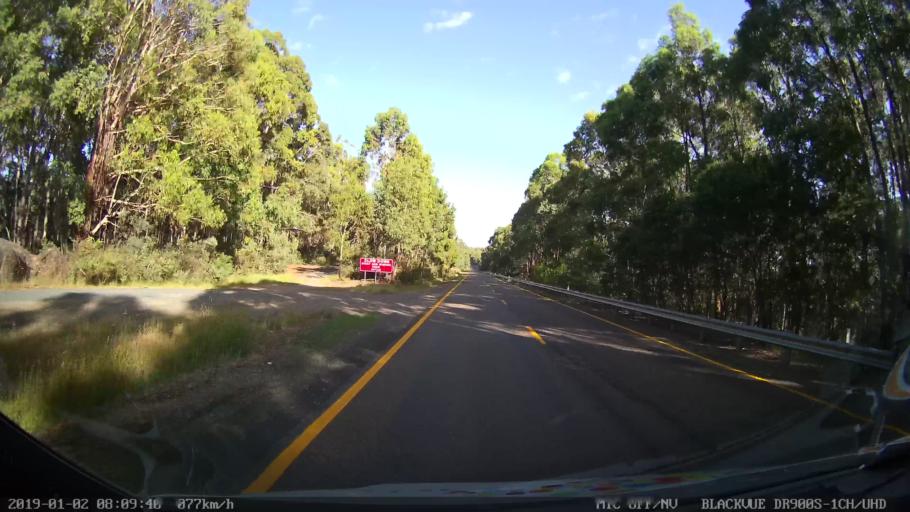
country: AU
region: New South Wales
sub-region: Tumut Shire
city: Tumut
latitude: -35.6048
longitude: 148.3776
